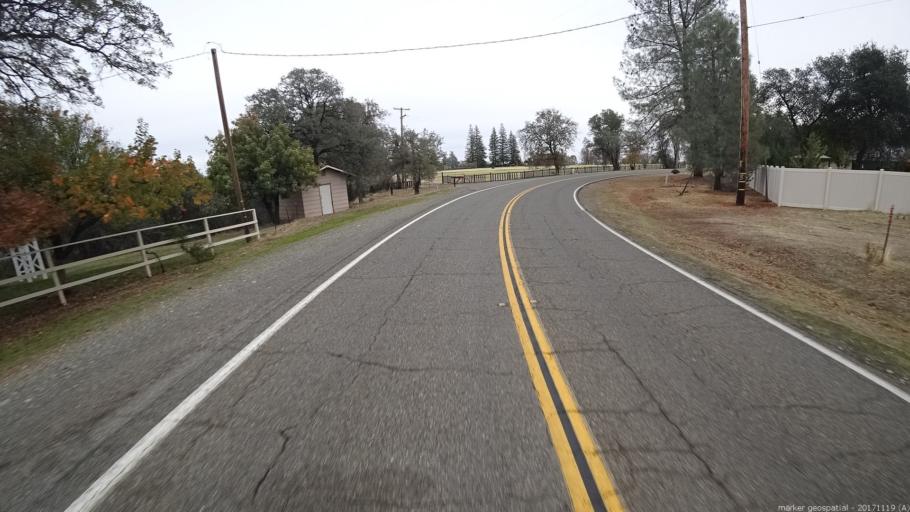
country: US
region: California
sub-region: Shasta County
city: Redding
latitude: 40.4878
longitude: -122.4456
